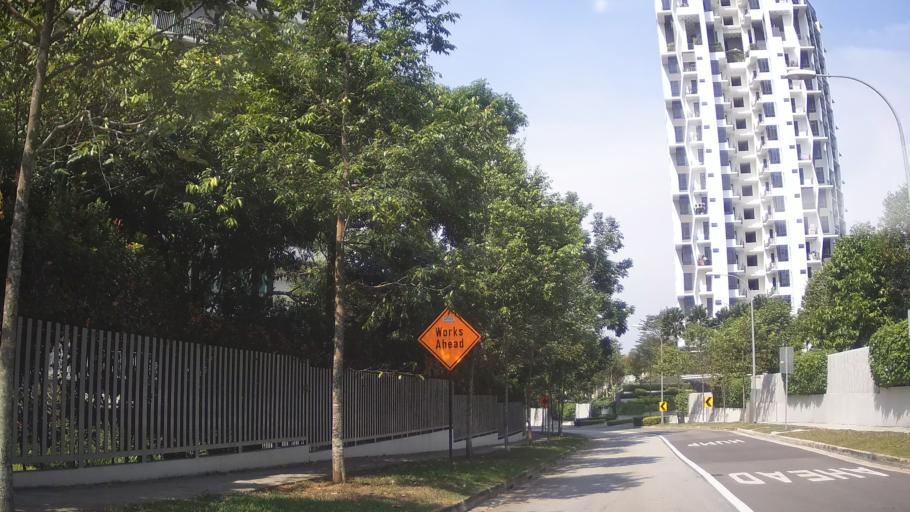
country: MY
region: Johor
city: Johor Bahru
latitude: 1.3710
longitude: 103.7774
